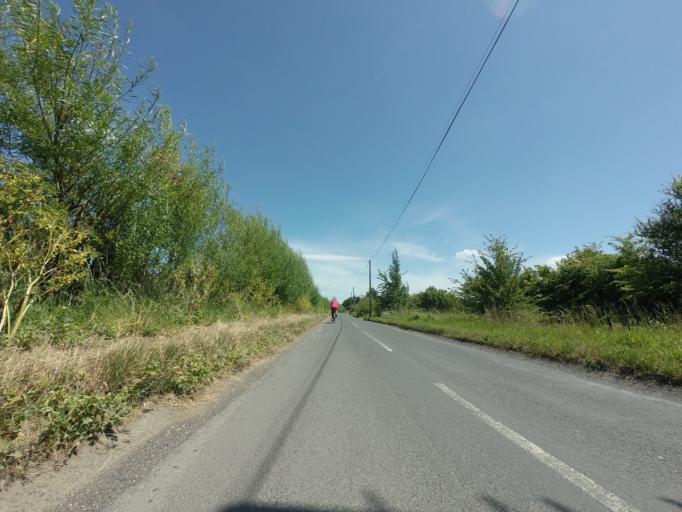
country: GB
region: England
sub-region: Medway
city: Cooling
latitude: 51.4541
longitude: 0.5126
